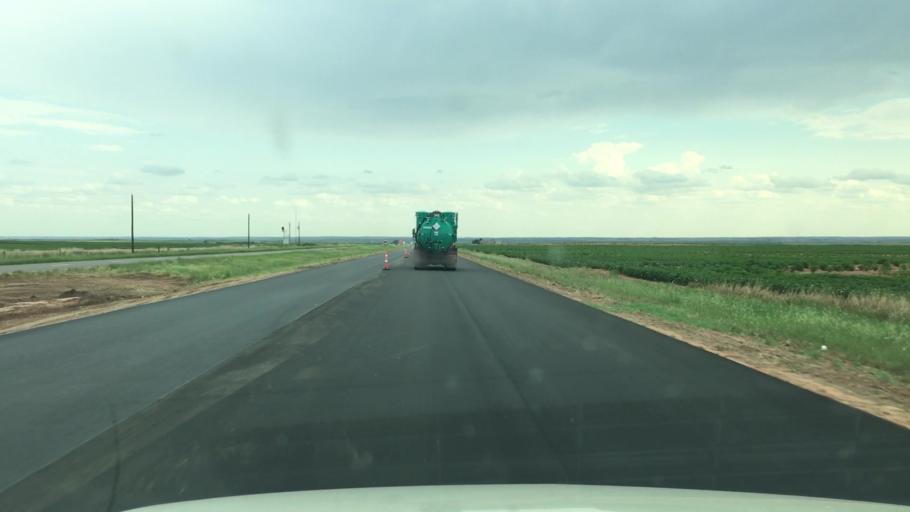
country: US
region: Texas
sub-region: Hall County
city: Memphis
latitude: 34.6284
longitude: -100.4752
